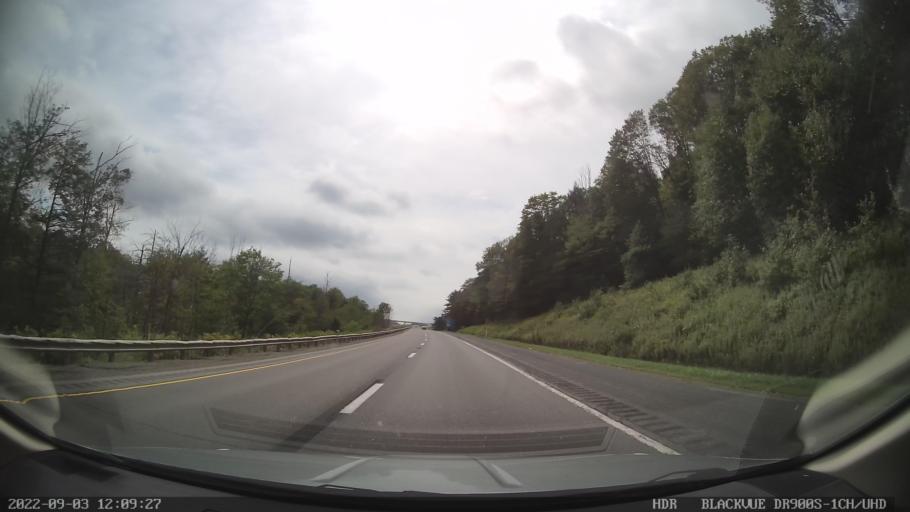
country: US
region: Pennsylvania
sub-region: Tioga County
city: Blossburg
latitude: 41.4671
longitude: -77.1371
